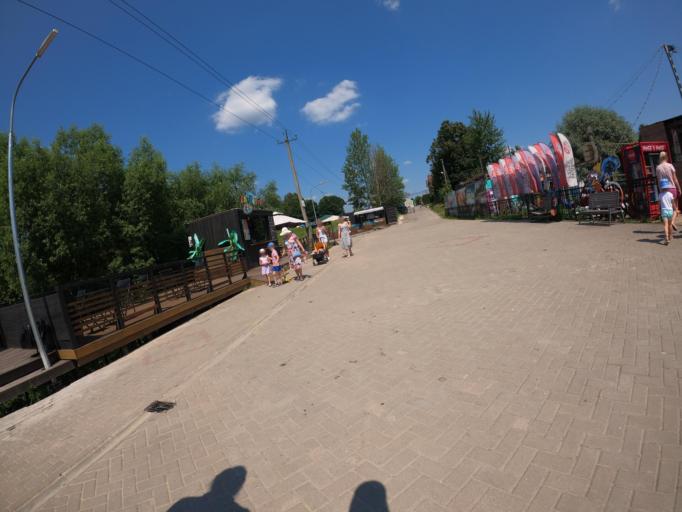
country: RU
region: Kaluga
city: Obninsk
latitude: 55.1238
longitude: 36.5947
